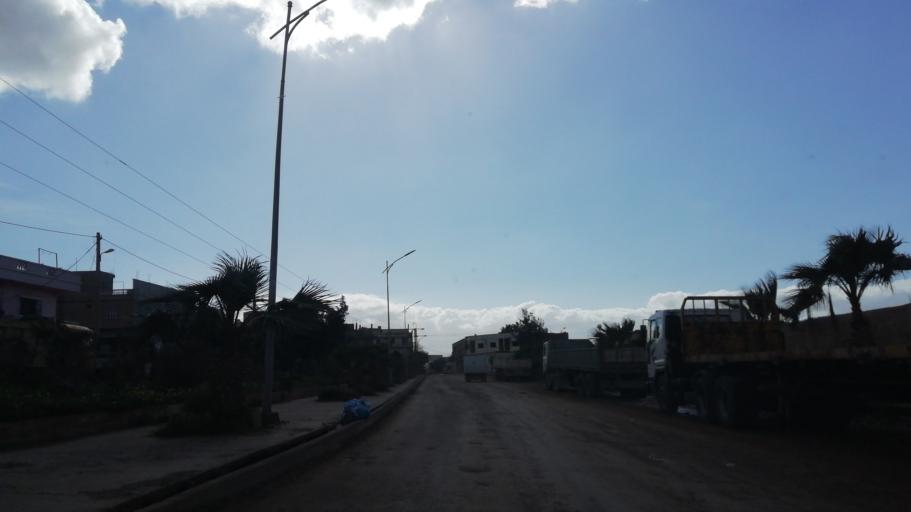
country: DZ
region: Oran
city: Es Senia
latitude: 35.6239
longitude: -0.5841
